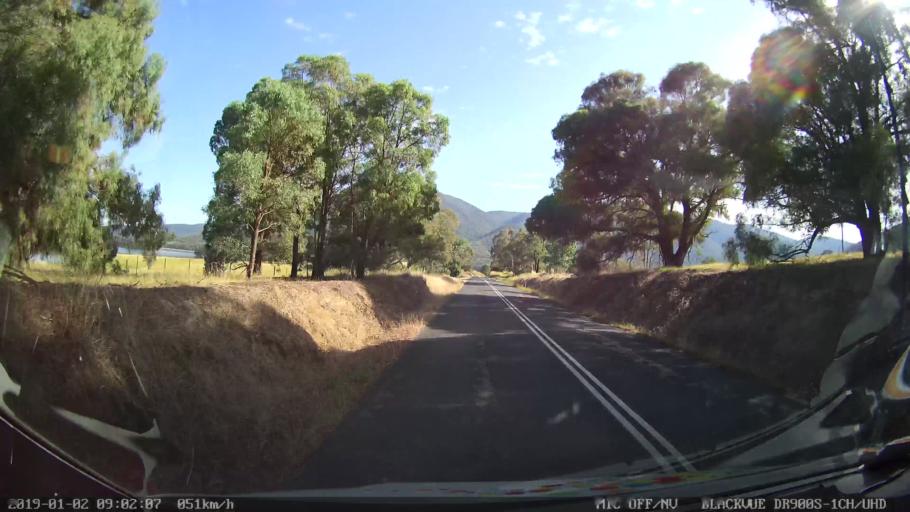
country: AU
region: New South Wales
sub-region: Tumut Shire
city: Tumut
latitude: -35.5756
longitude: 148.3108
